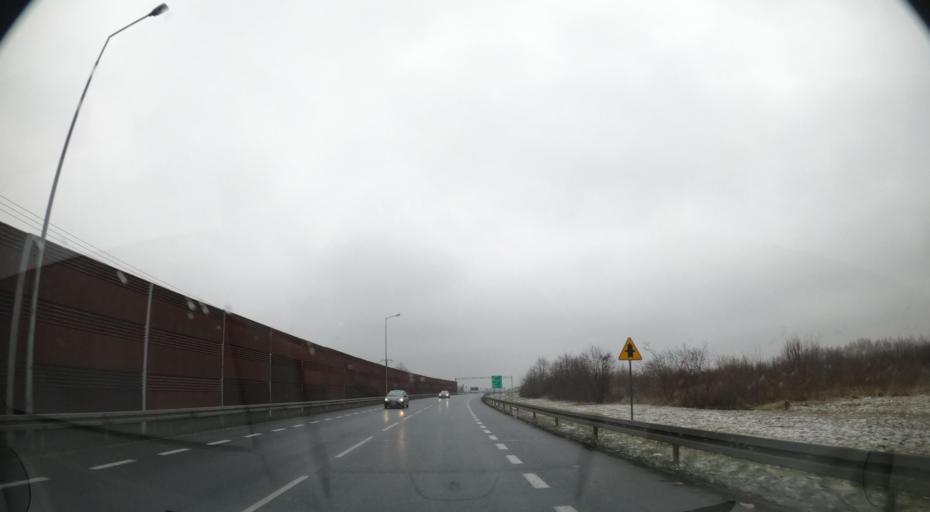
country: PL
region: Masovian Voivodeship
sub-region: Powiat sochaczewski
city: Sochaczew
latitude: 52.2090
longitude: 20.2493
